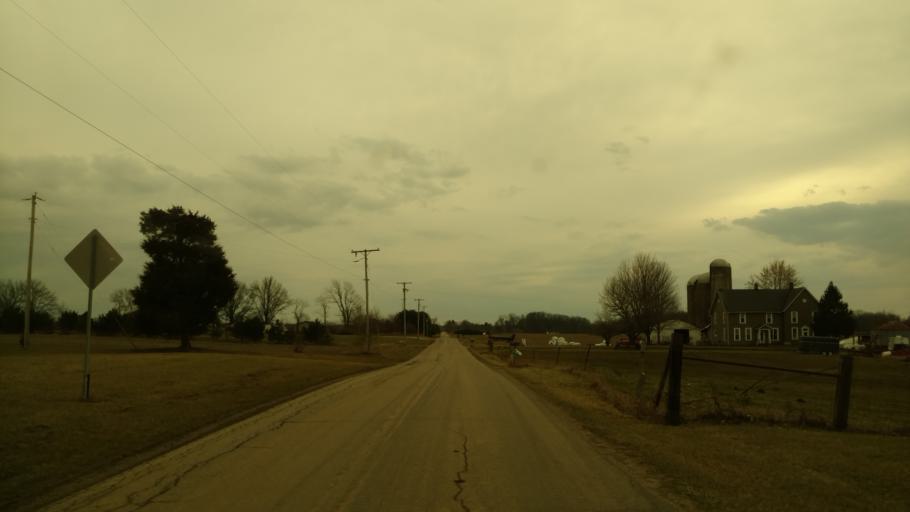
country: US
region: Ohio
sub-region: Crawford County
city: Crestline
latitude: 40.7561
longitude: -82.6983
